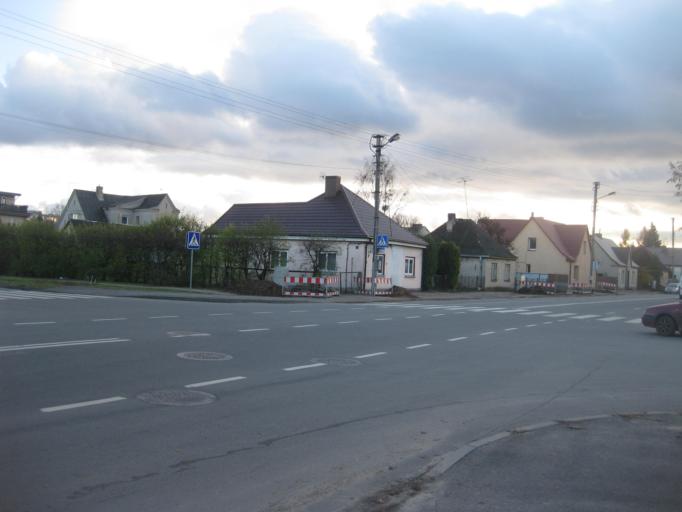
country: LT
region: Kauno apskritis
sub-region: Kaunas
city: Silainiai
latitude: 54.9199
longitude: 23.8982
